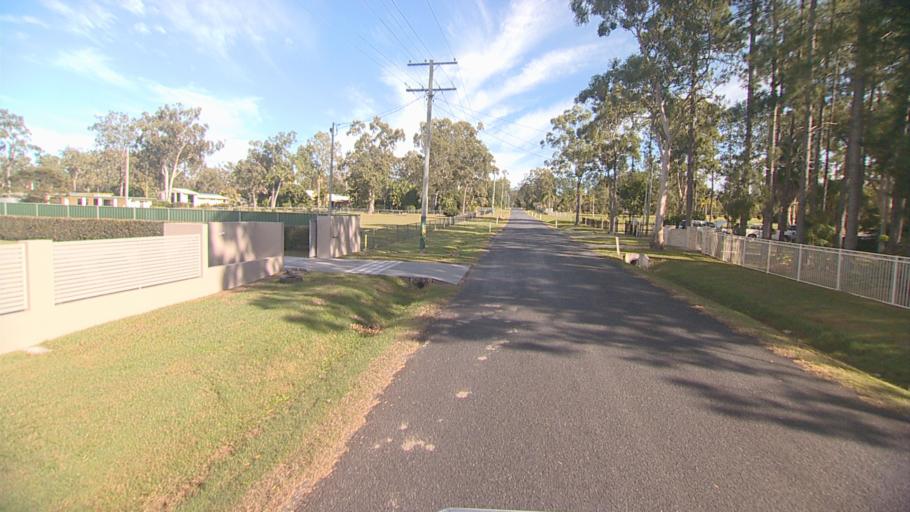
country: AU
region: Queensland
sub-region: Brisbane
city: Forest Lake
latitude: -27.6579
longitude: 152.9879
